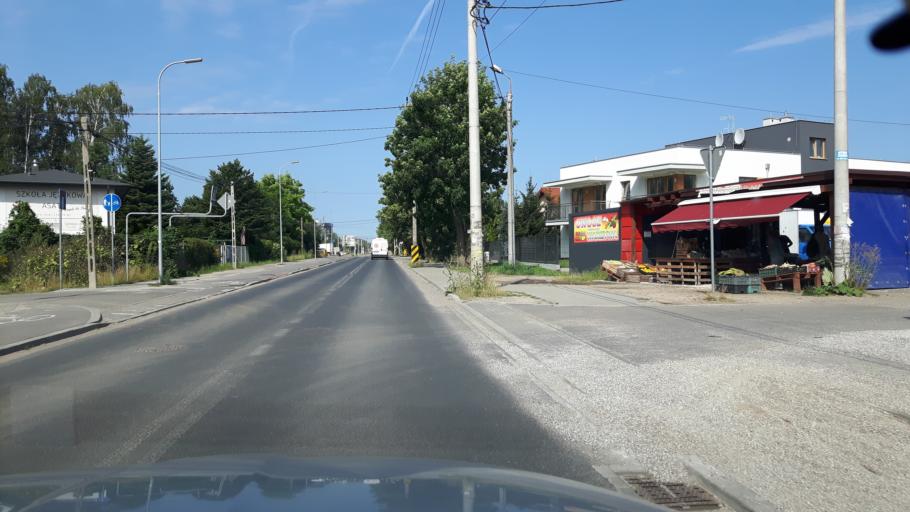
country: PL
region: Masovian Voivodeship
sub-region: Powiat wolominski
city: Marki
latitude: 52.3208
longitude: 21.0918
